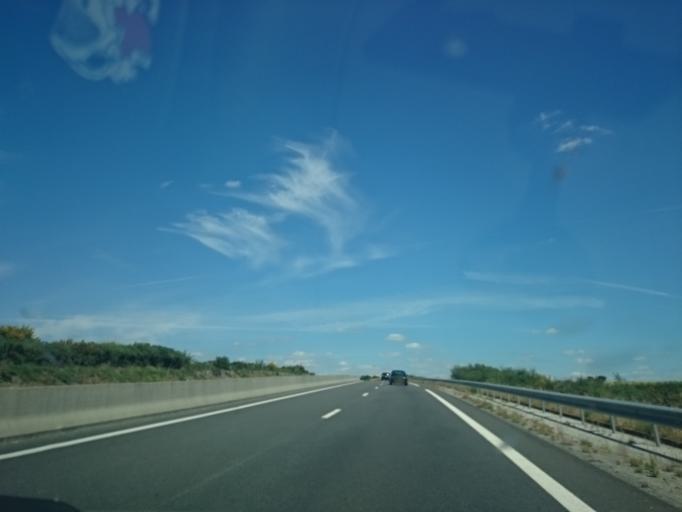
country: FR
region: Brittany
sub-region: Departement des Cotes-d'Armor
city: Gouarec
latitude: 48.2313
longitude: -3.1548
